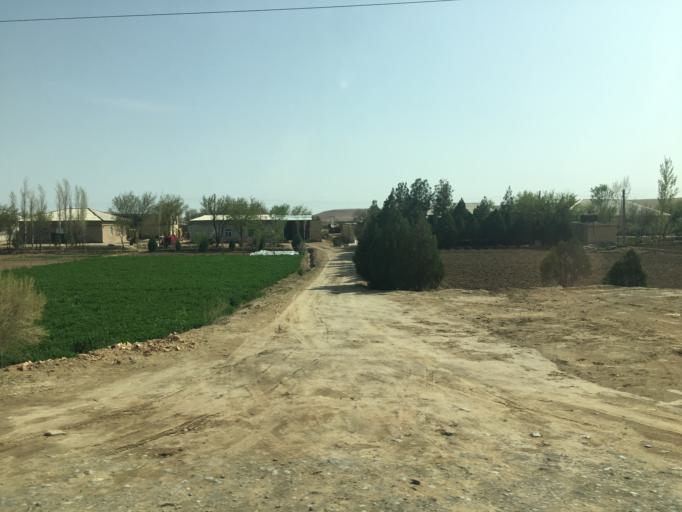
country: TM
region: Mary
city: Seydi
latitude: 39.4100
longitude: 62.9967
